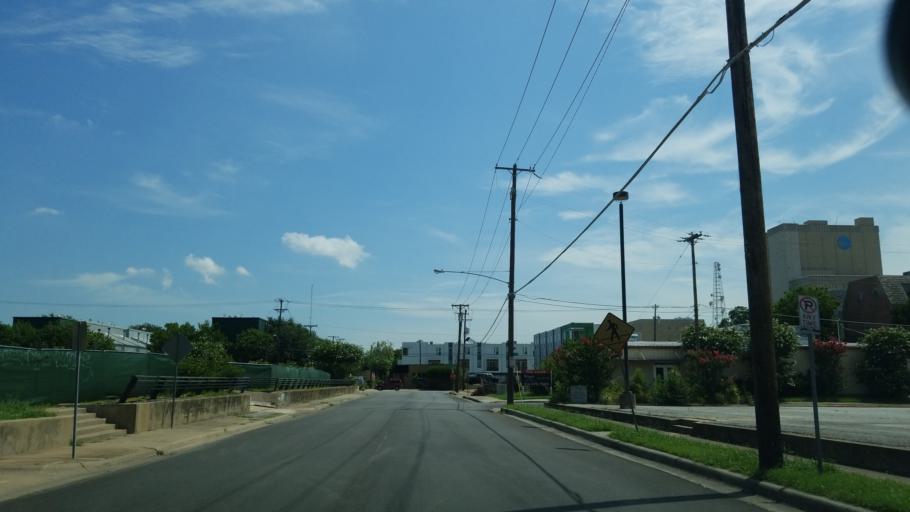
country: US
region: Texas
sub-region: Dallas County
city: Dallas
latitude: 32.7964
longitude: -96.7861
